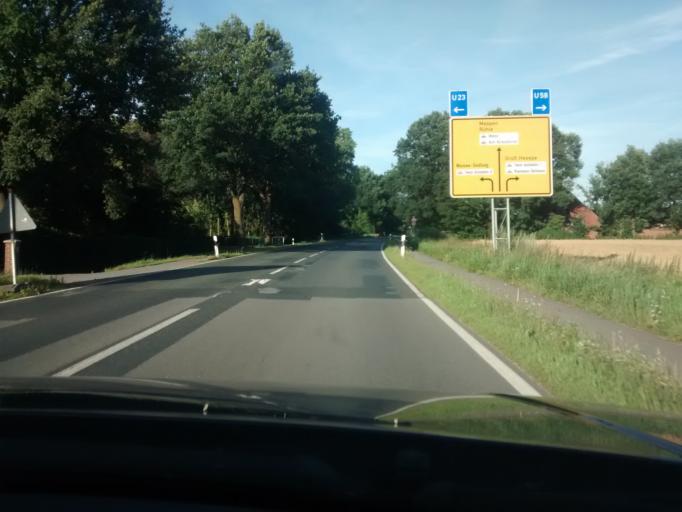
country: DE
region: Lower Saxony
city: Geeste
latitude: 52.6679
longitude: 7.1827
